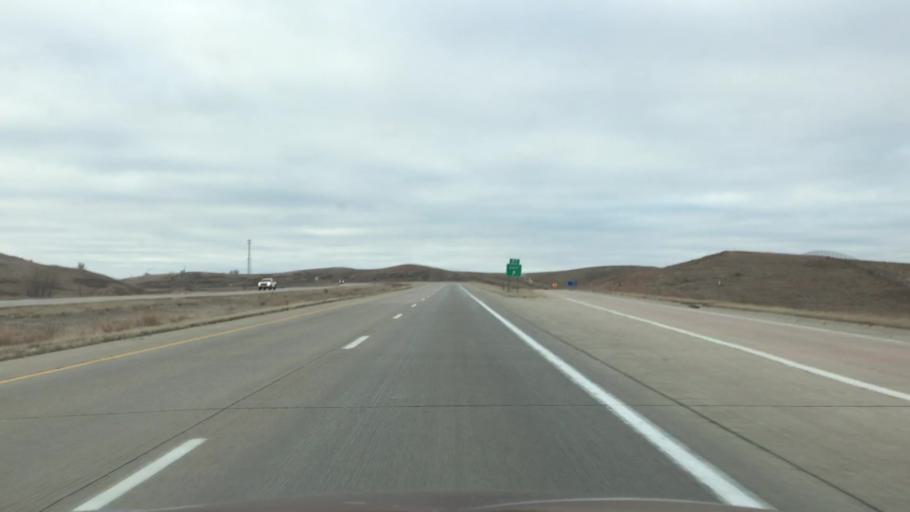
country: US
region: Iowa
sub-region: Woodbury County
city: Sioux City
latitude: 42.5235
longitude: -96.3395
